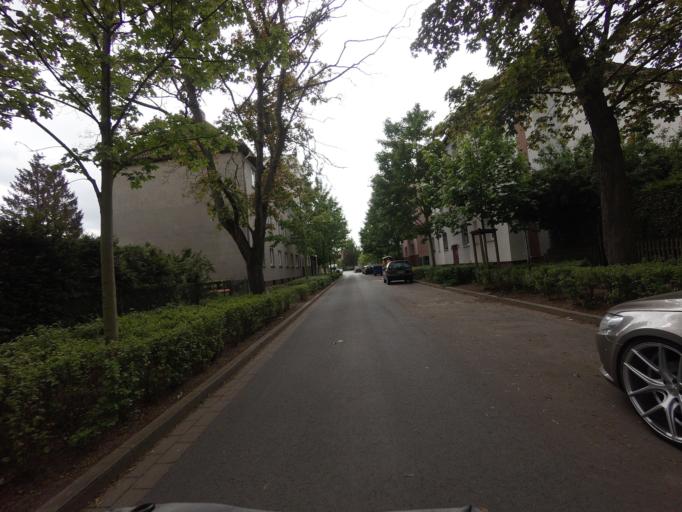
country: DE
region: Lower Saxony
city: Braunschweig
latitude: 52.2889
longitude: 10.5331
